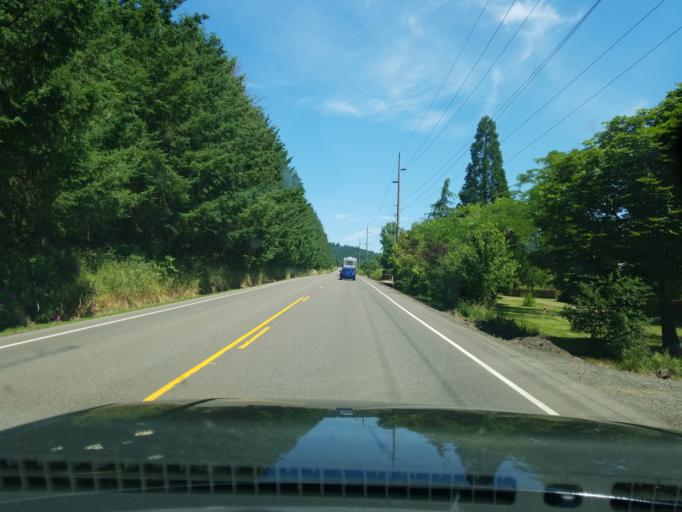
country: US
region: Oregon
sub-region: Yamhill County
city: Yamhill
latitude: 45.3638
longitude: -123.1670
